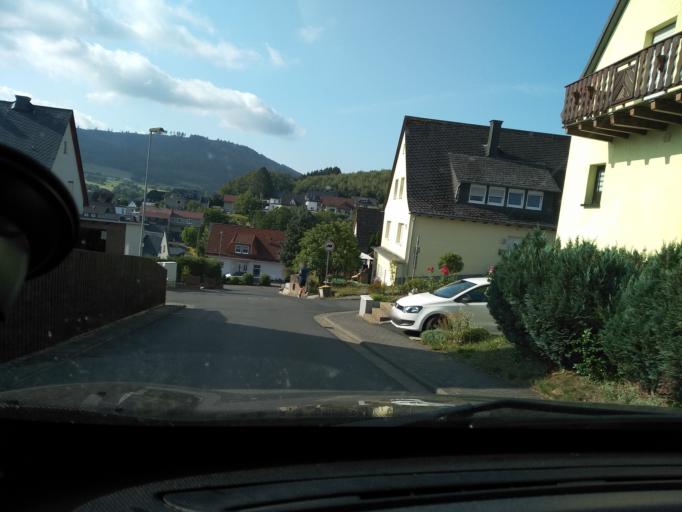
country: DE
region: Hesse
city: Dillenburg
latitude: 50.8113
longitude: 8.3360
